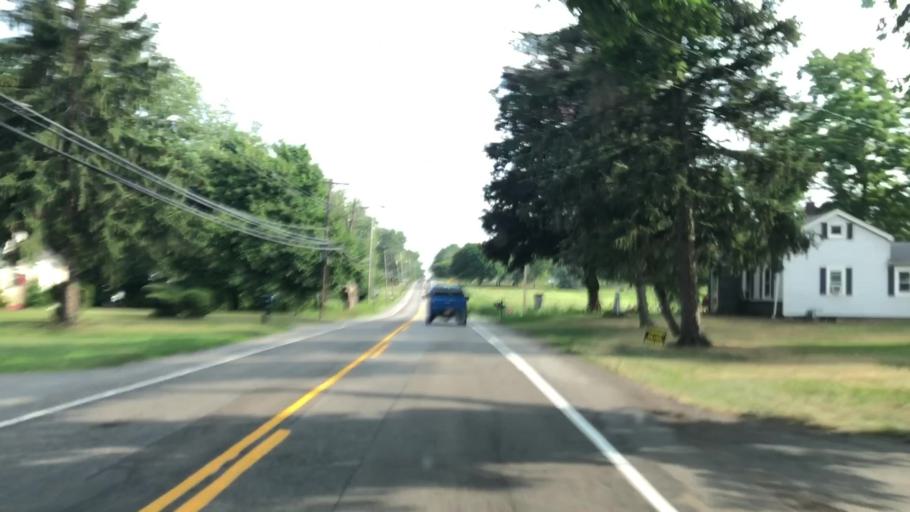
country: US
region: New York
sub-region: Erie County
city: Elma Center
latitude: 42.8262
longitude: -78.6367
